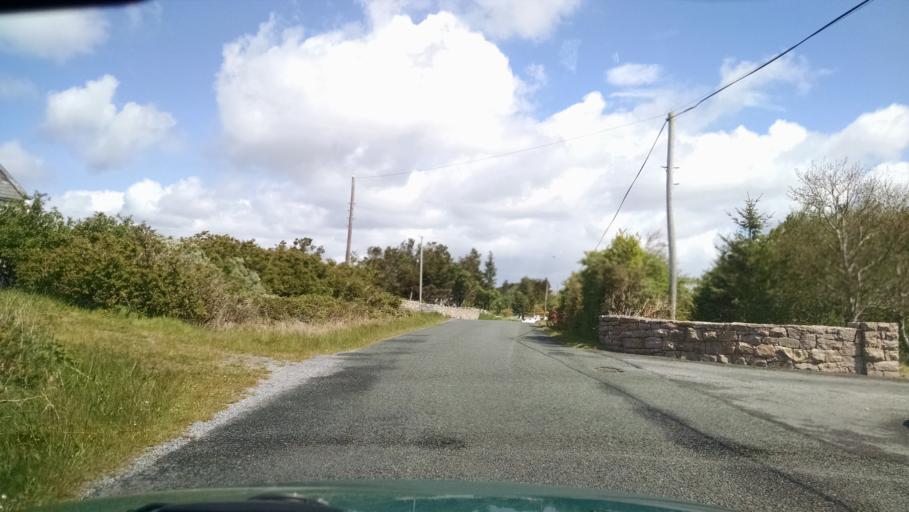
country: IE
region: Connaught
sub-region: County Galway
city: Oughterard
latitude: 53.2527
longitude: -9.6170
